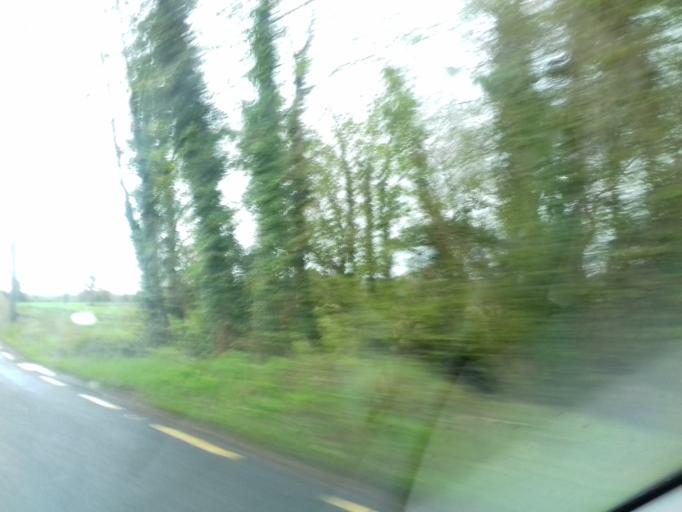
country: IE
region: Ulster
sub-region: An Cabhan
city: Ballyconnell
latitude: 54.1349
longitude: -7.6938
